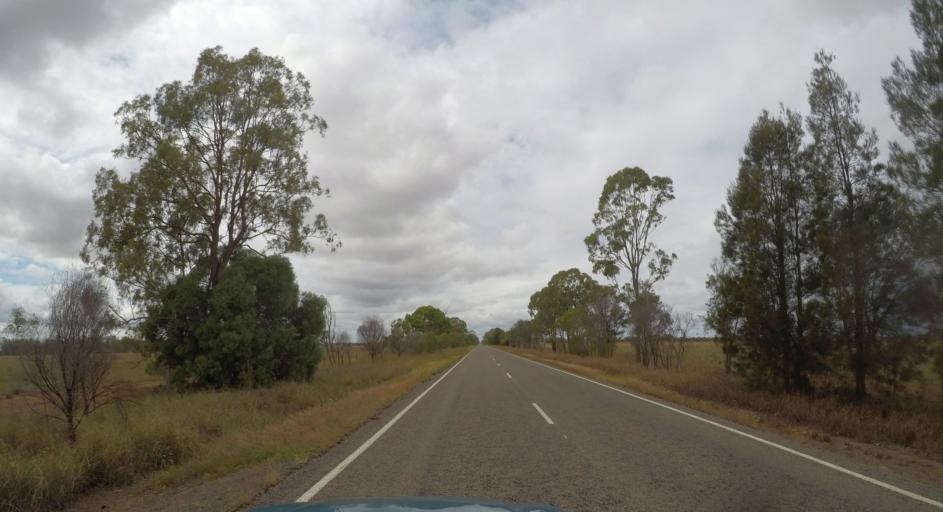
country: AU
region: Queensland
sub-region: South Burnett
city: Kingaroy
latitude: -26.3915
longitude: 151.2137
